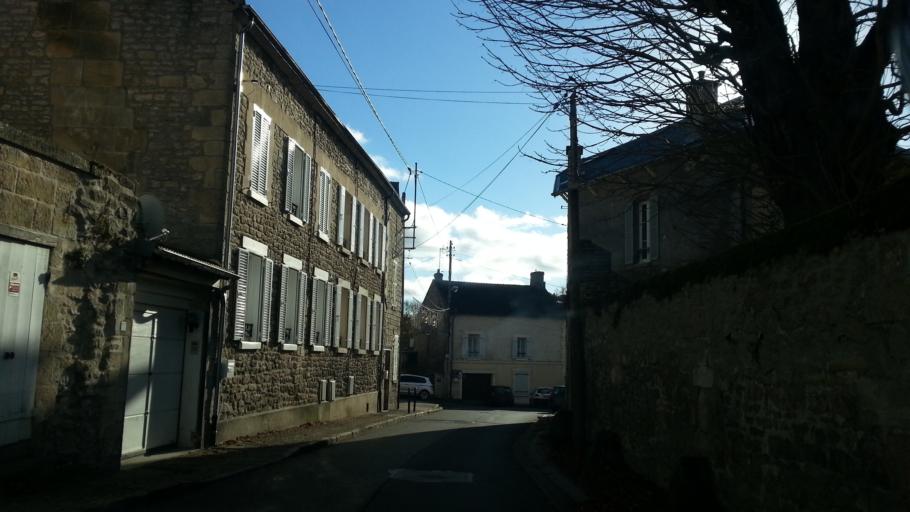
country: FR
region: Picardie
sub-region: Departement de l'Oise
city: Gouvieux
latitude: 49.1990
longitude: 2.4321
